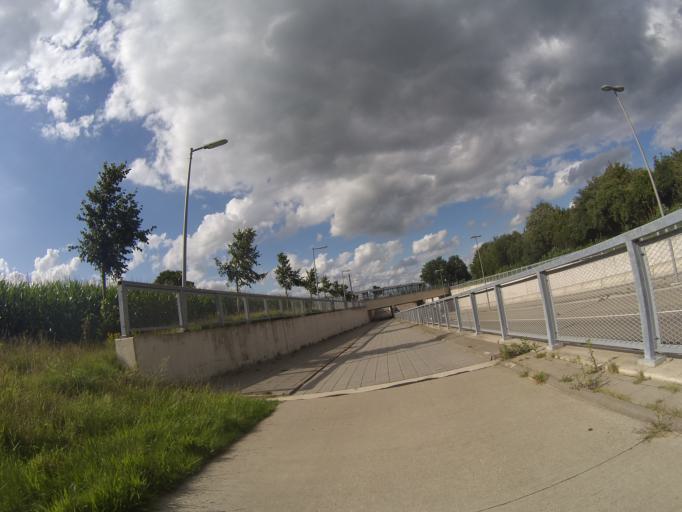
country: NL
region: Drenthe
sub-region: Gemeente Emmen
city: Emmen
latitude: 52.7481
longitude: 6.8747
